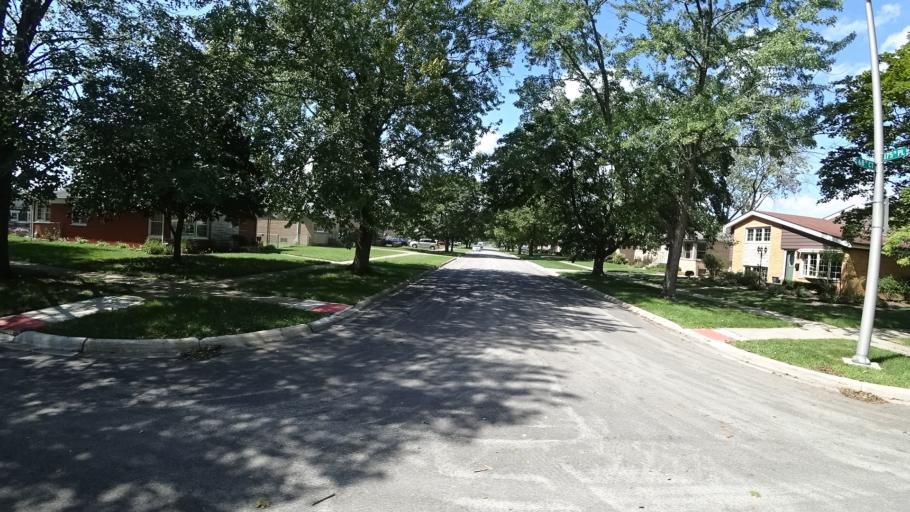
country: US
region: Illinois
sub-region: Cook County
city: Tinley Park
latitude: 41.5723
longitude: -87.7856
